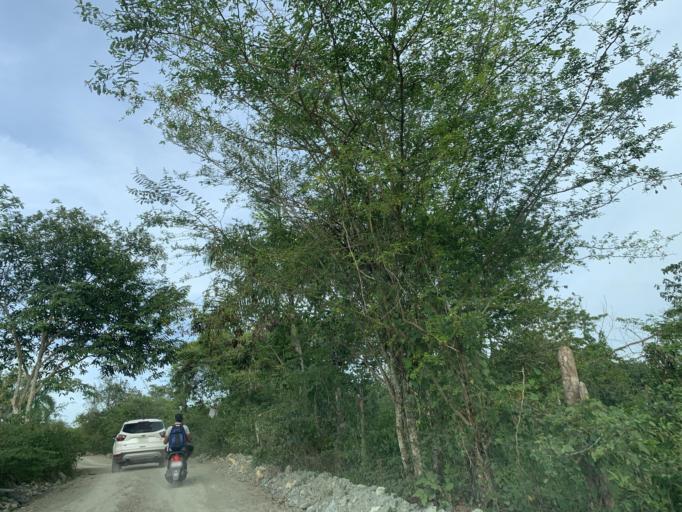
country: DO
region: Santiago
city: Pedro Garcia
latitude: 19.6980
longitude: -70.6170
